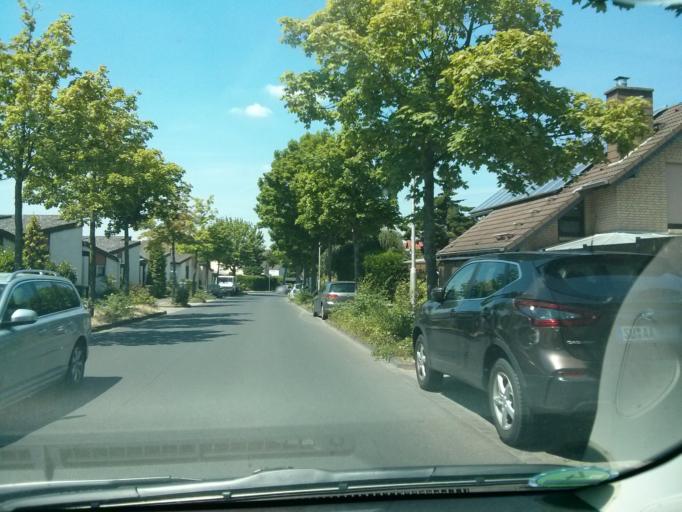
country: DE
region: North Rhine-Westphalia
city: Meckenheim
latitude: 50.6261
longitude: 7.0492
